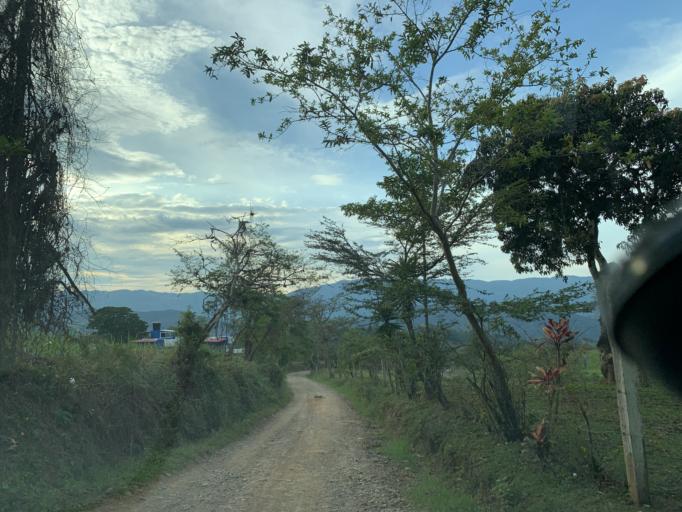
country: CO
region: Boyaca
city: Santana
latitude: 6.0803
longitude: -73.4910
